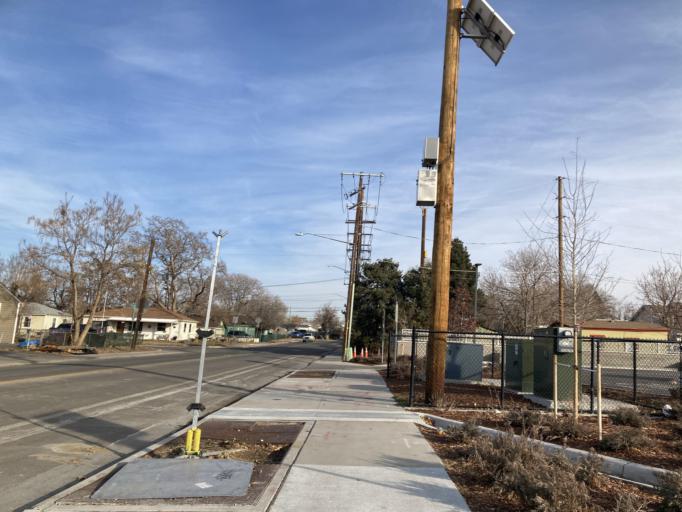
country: US
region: Colorado
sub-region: Adams County
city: Commerce City
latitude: 39.7819
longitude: -104.9558
